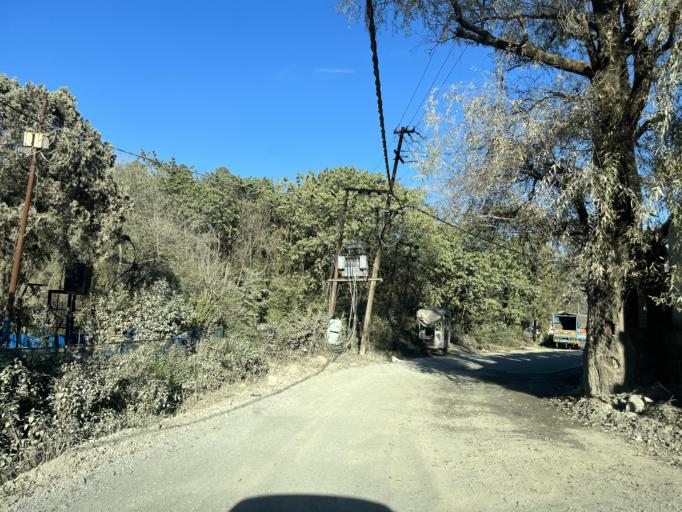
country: IN
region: Uttarakhand
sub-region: Naini Tal
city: Bhim Tal
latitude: 29.3504
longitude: 79.5530
